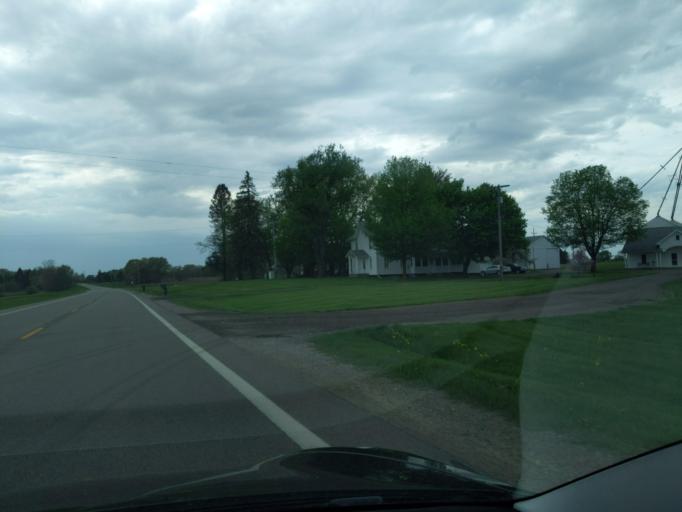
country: US
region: Michigan
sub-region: Ingham County
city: Stockbridge
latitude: 42.4121
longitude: -84.1335
